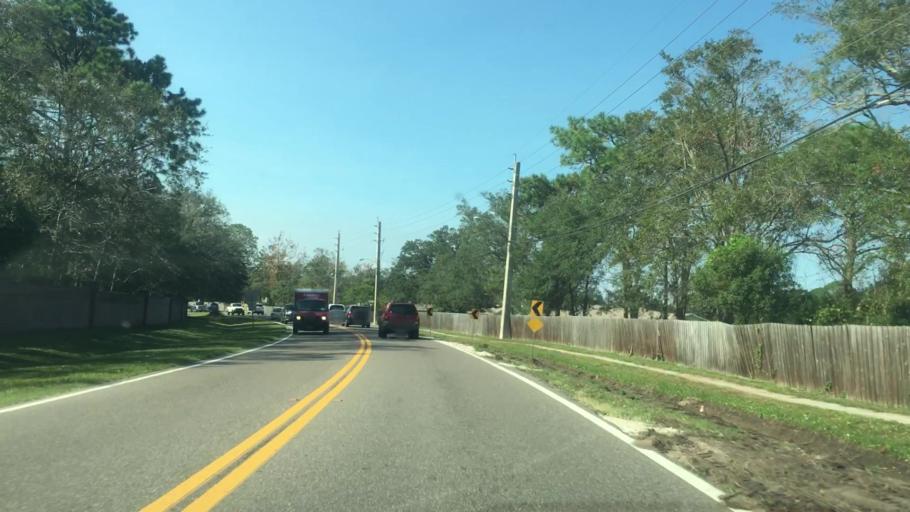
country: US
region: Florida
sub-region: Duval County
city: Neptune Beach
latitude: 30.2985
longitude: -81.4380
